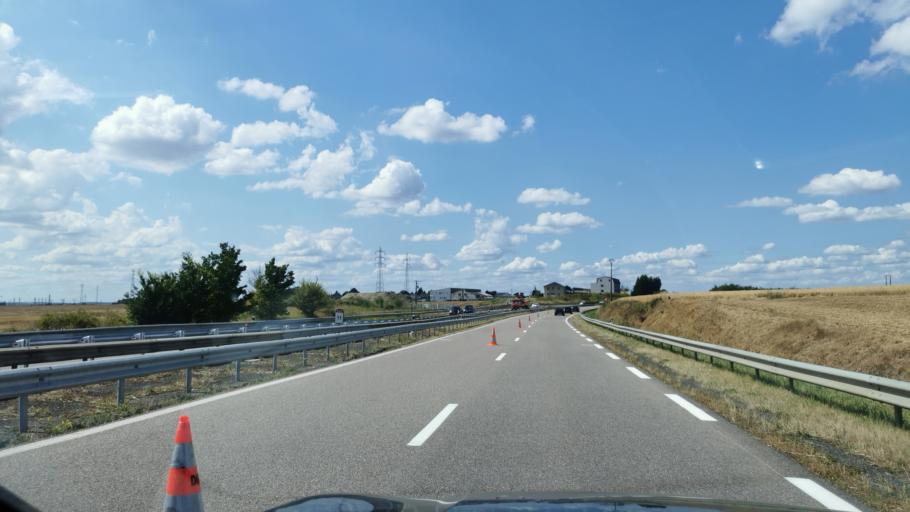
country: FR
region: Lorraine
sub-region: Departement de Meurthe-et-Moselle
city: Villers-la-Montagne
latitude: 49.4820
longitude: 5.8181
